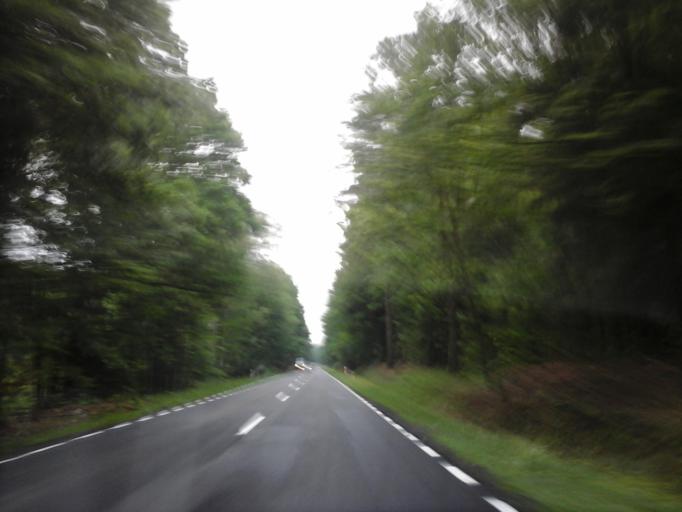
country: PL
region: West Pomeranian Voivodeship
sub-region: Powiat szczecinecki
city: Lubowo
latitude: 53.5901
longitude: 16.3177
